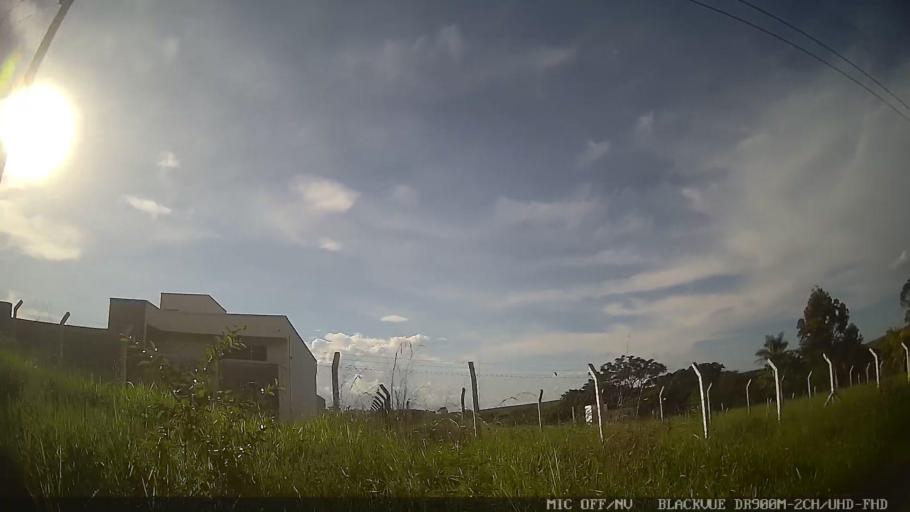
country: BR
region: Sao Paulo
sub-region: Tiete
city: Tiete
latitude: -23.0870
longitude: -47.6952
